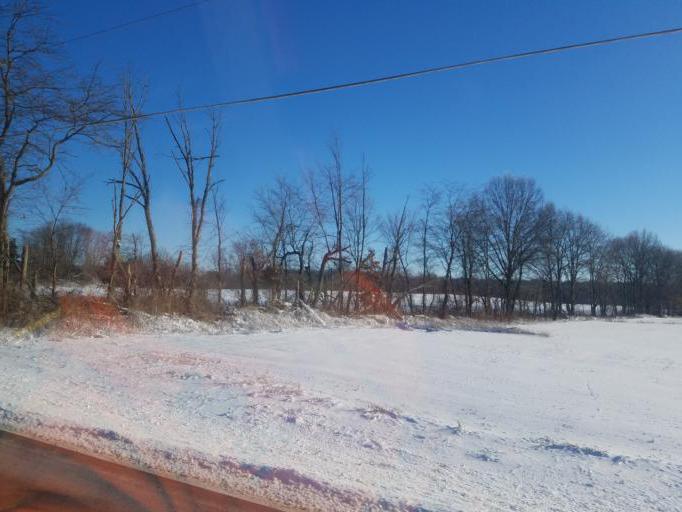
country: US
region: Ohio
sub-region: Delaware County
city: Sunbury
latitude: 40.2958
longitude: -82.9101
